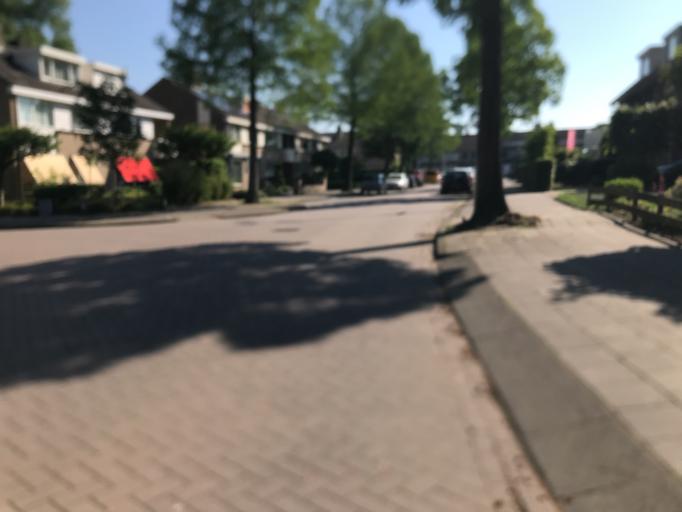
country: NL
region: North Brabant
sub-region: Gemeente Waalre
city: Waalre
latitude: 51.4152
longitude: 5.4343
